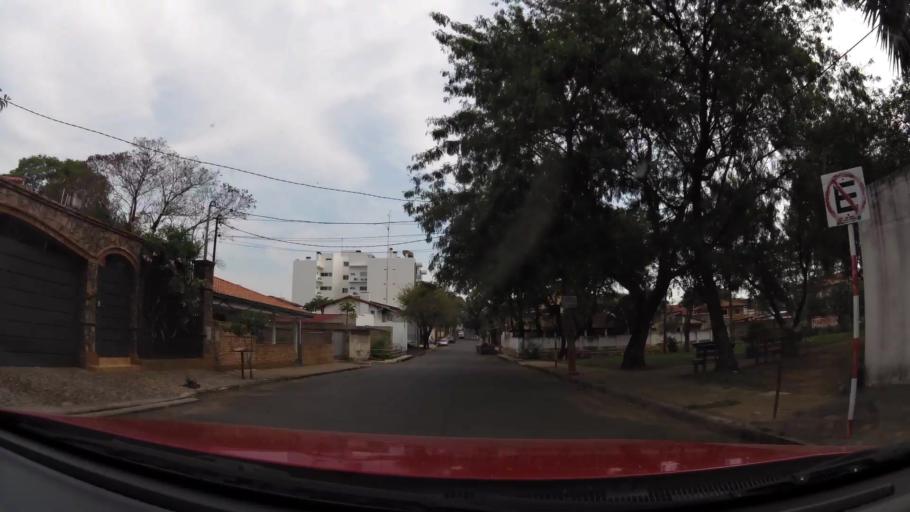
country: PY
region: Asuncion
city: Asuncion
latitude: -25.2883
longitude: -57.5878
